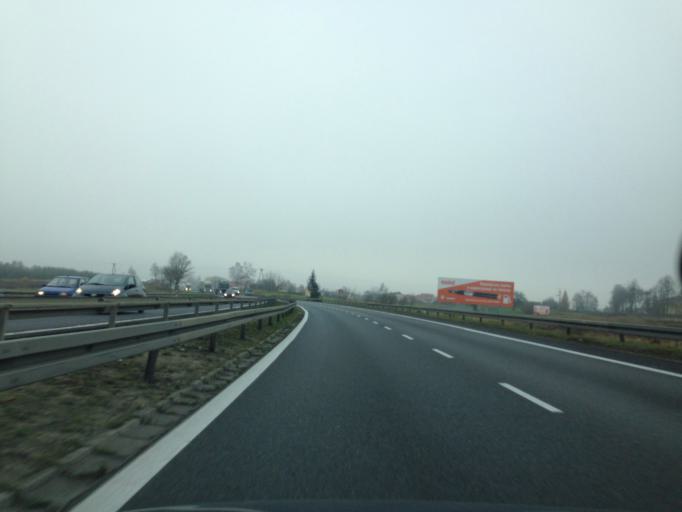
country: PL
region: Silesian Voivodeship
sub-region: Powiat czestochowski
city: Kamienica Polska
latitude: 50.6341
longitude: 19.1360
